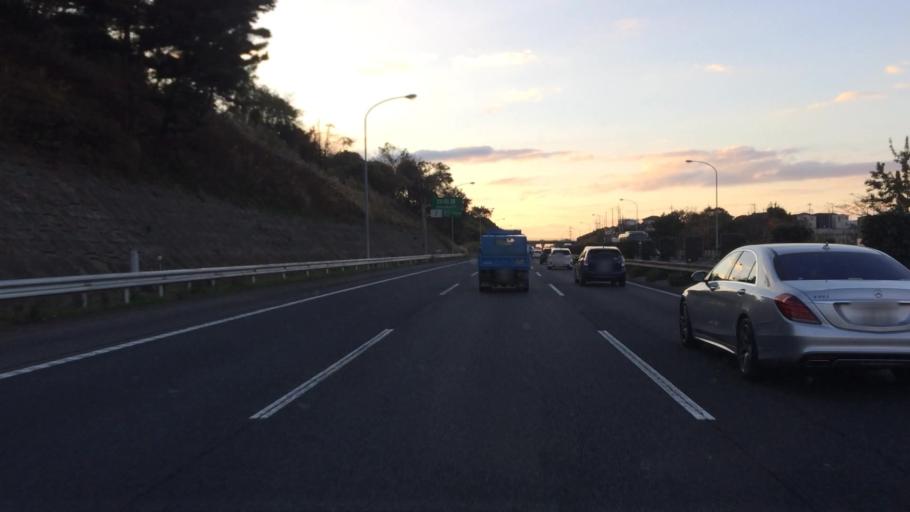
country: JP
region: Chiba
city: Yotsukaido
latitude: 35.6828
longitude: 140.1932
